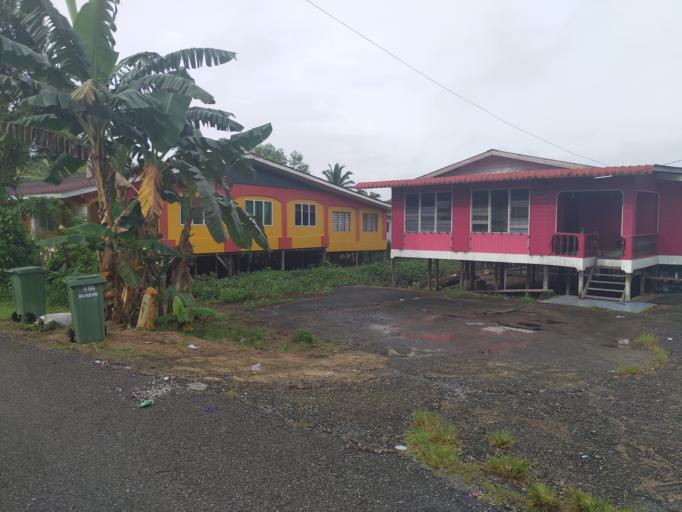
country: MY
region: Sarawak
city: Sibu
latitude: 2.8922
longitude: 112.1013
